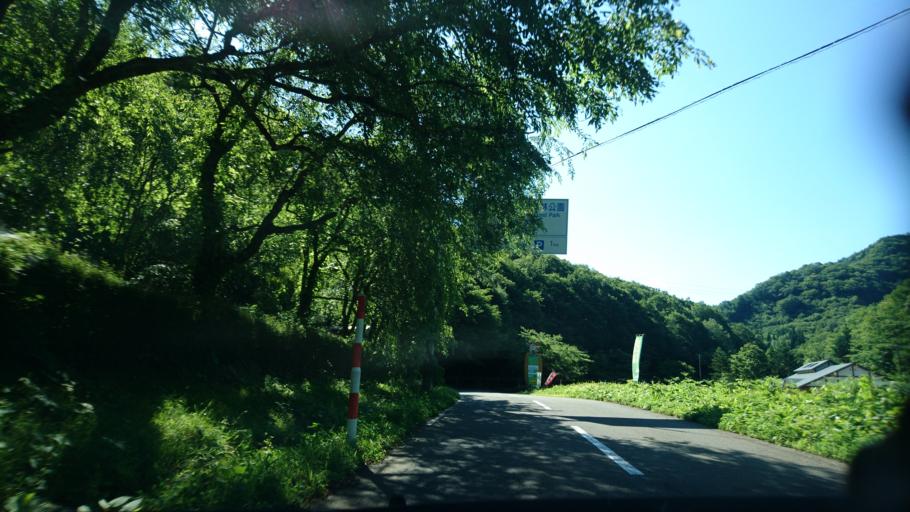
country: JP
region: Akita
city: Kakunodatemachi
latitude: 39.7154
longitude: 140.6254
